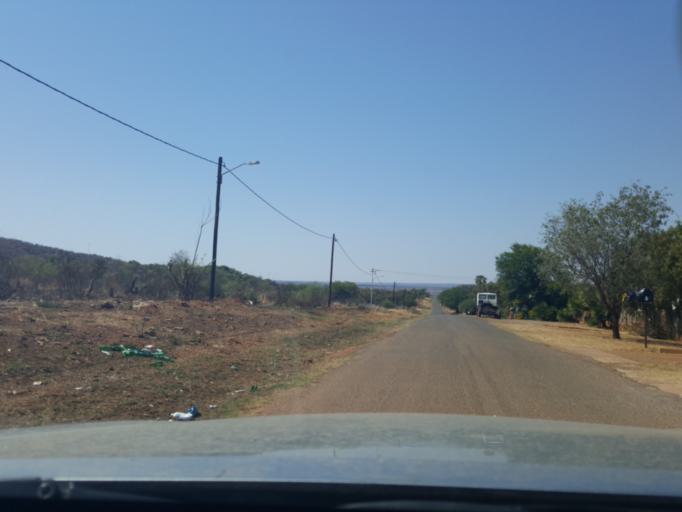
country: ZA
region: North-West
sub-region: Ngaka Modiri Molema District Municipality
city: Zeerust
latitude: -25.5258
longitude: 26.0800
